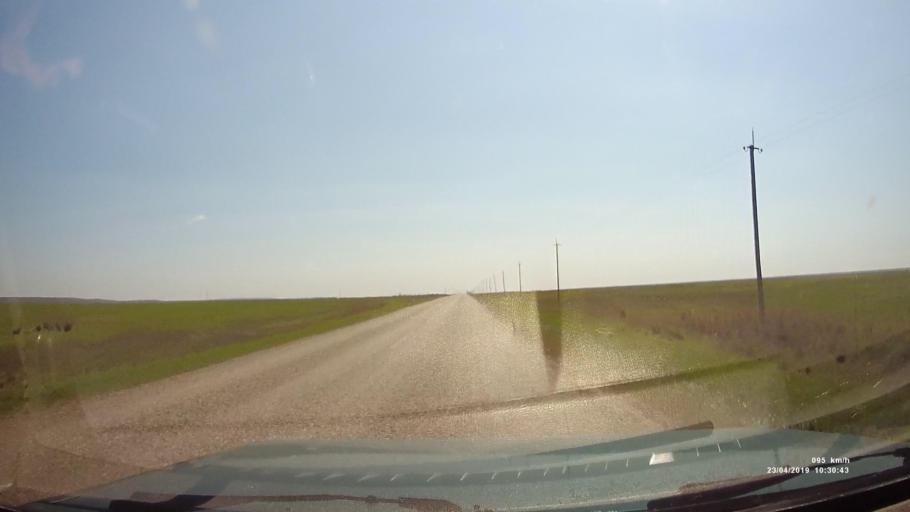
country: RU
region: Kalmykiya
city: Yashalta
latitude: 46.5903
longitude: 42.5495
